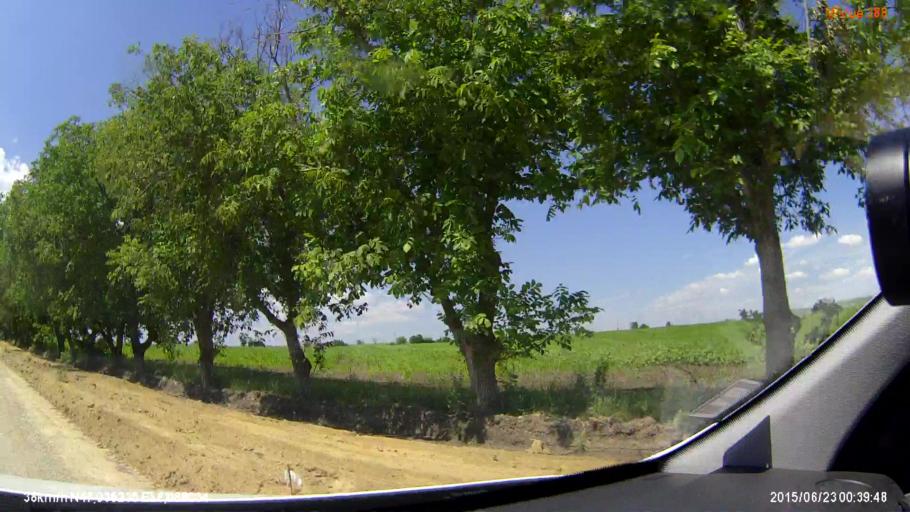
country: RO
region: Iasi
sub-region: Comuna Grozesti
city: Grozesti
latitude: 47.0352
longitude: 28.0384
